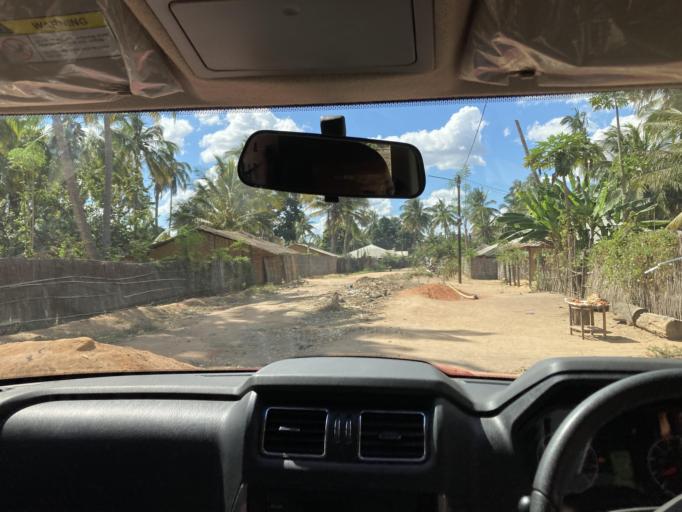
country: MZ
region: Cabo Delgado
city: Montepuez
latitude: -13.1374
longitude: 39.0016
